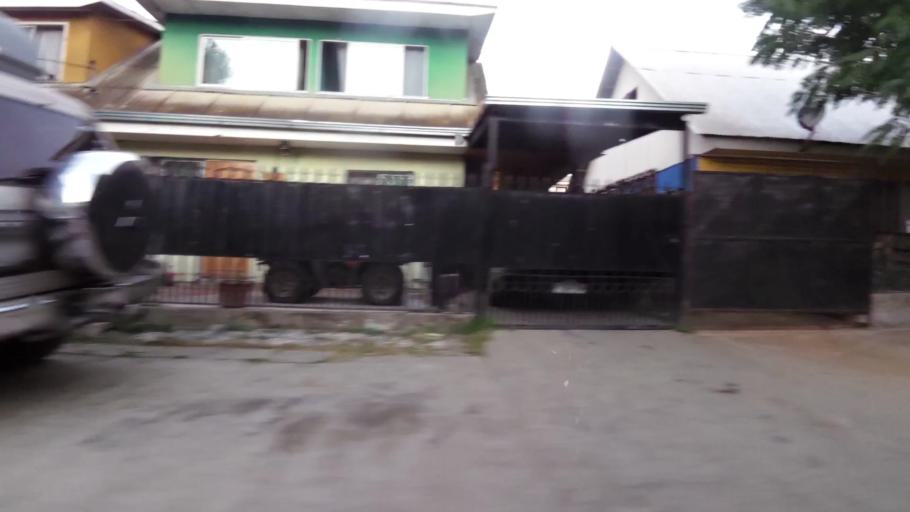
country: CL
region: Maule
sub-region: Provincia de Talca
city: Talca
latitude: -35.4512
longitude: -71.6286
